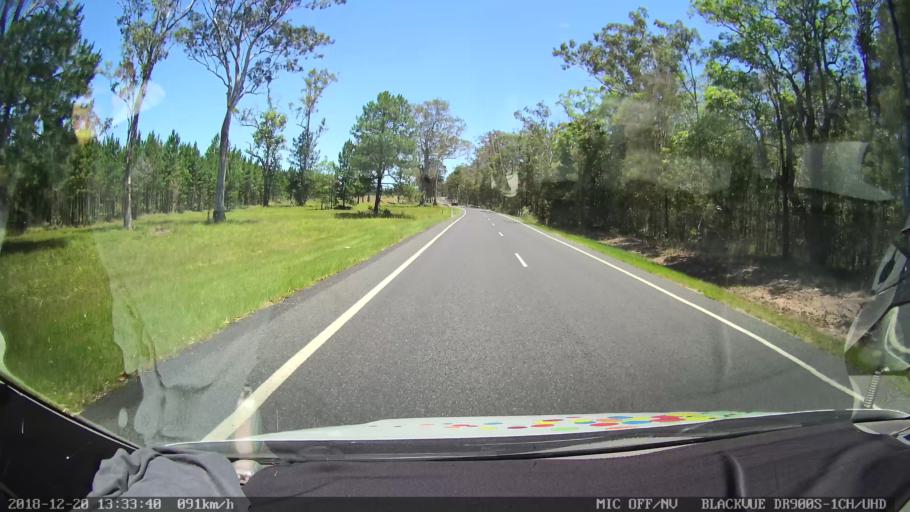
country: AU
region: New South Wales
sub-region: Clarence Valley
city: Gordon
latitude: -29.2486
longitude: 152.9856
